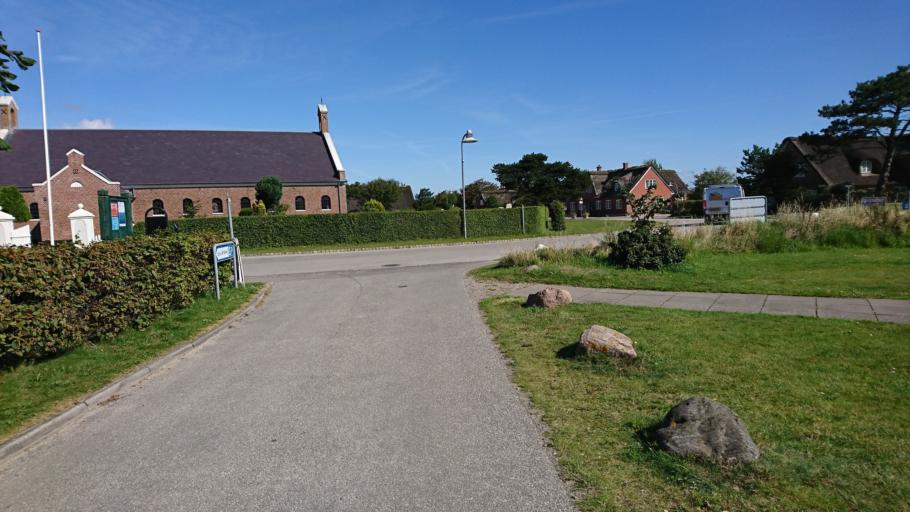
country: DK
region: South Denmark
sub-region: Fano Kommune
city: Nordby
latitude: 55.3492
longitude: 8.4669
